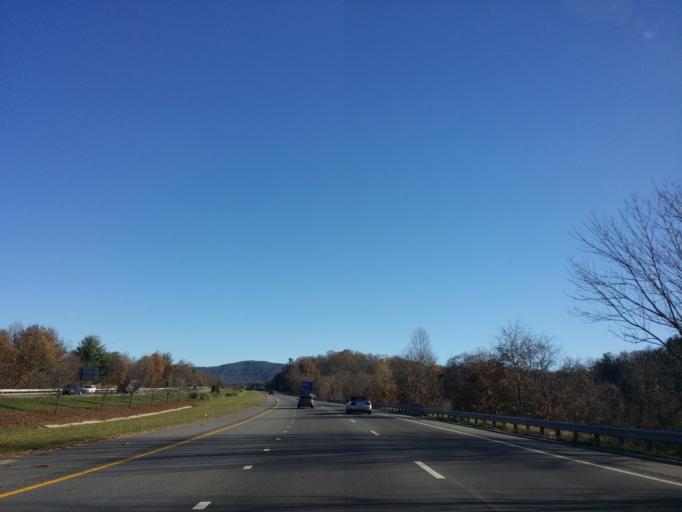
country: US
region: North Carolina
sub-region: Buncombe County
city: Asheville
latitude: 35.5768
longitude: -82.5184
